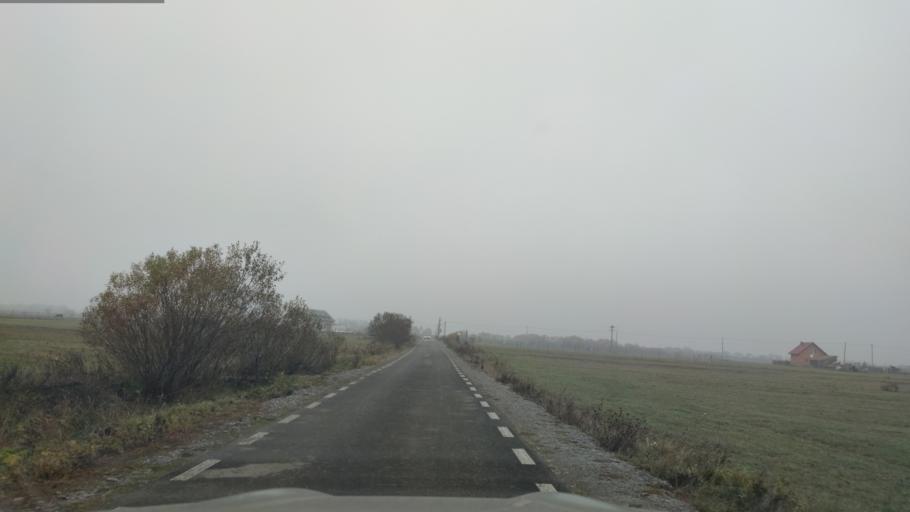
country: RO
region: Harghita
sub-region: Comuna Remetea
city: Remetea
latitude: 46.8080
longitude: 25.4229
